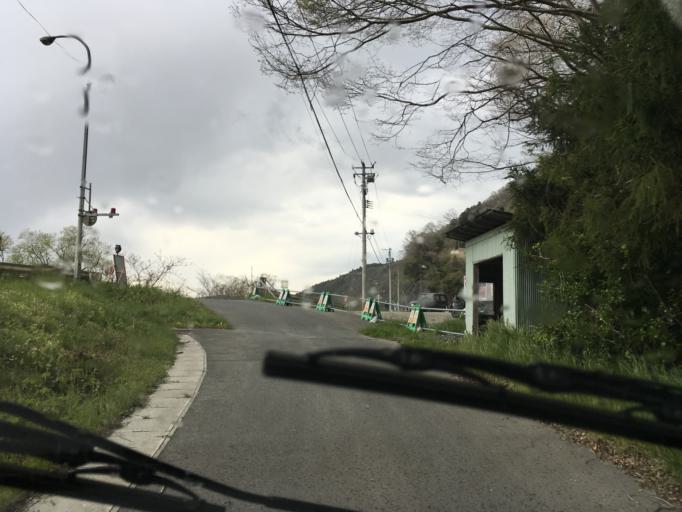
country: JP
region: Miyagi
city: Ishinomaki
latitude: 38.5551
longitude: 141.3082
